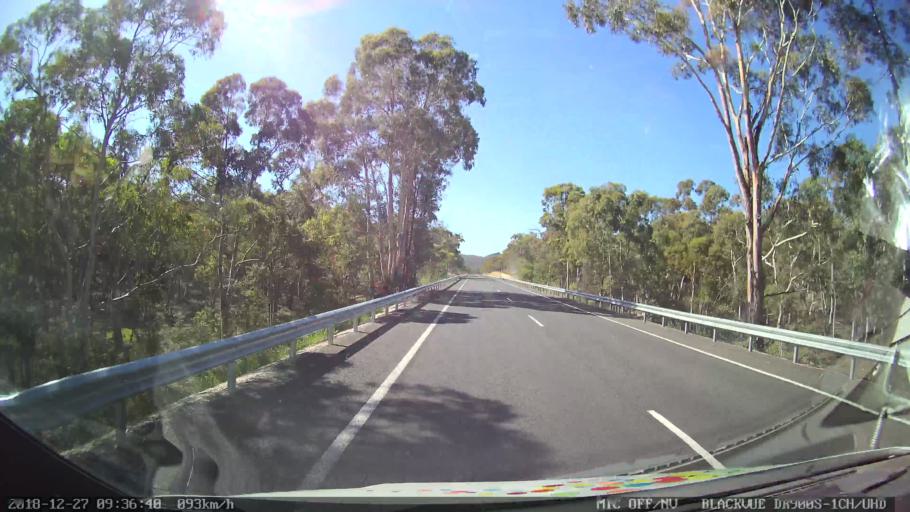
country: AU
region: New South Wales
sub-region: Lithgow
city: Portland
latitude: -33.2554
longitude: 150.0363
